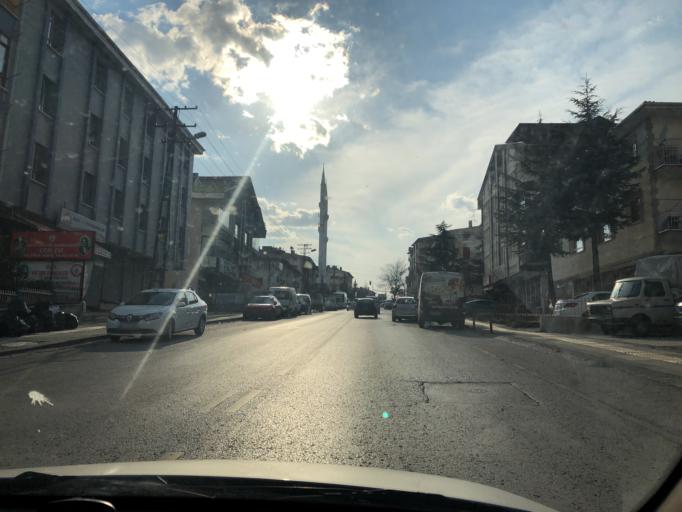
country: TR
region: Ankara
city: Ankara
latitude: 39.9852
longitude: 32.8487
